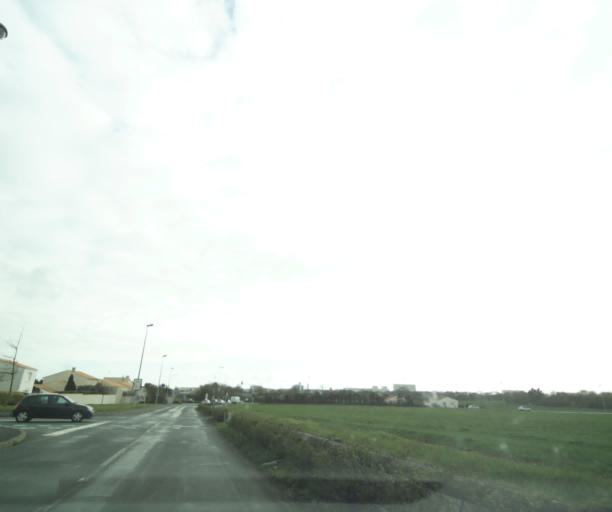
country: FR
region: Poitou-Charentes
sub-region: Departement de la Charente-Maritime
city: Lagord
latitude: 46.1822
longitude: -1.1669
